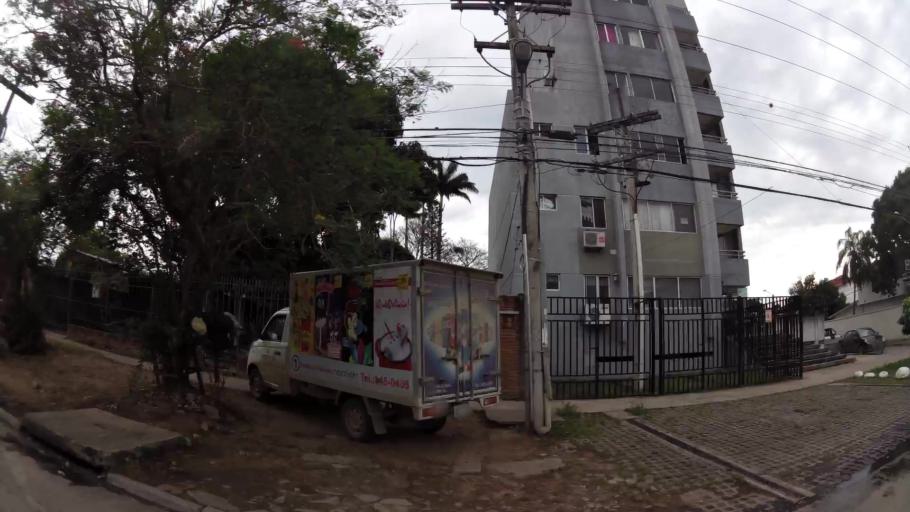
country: BO
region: Santa Cruz
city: Santa Cruz de la Sierra
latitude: -17.7580
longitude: -63.1765
